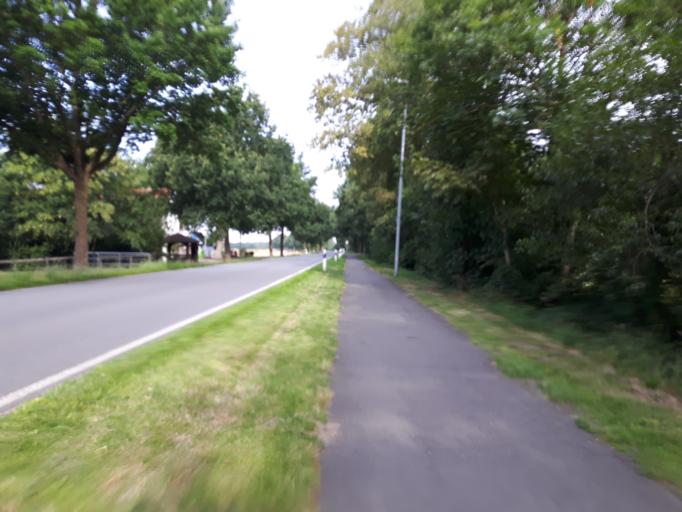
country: DE
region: Lower Saxony
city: Delmenhorst
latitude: 53.0872
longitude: 8.6154
